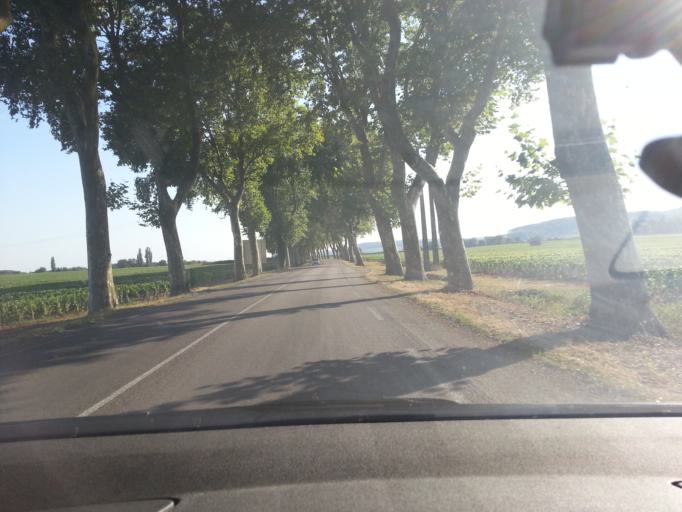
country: FR
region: Bourgogne
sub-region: Departement de la Cote-d'Or
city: Bligny-les-Beaune
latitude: 47.0115
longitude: 4.8117
